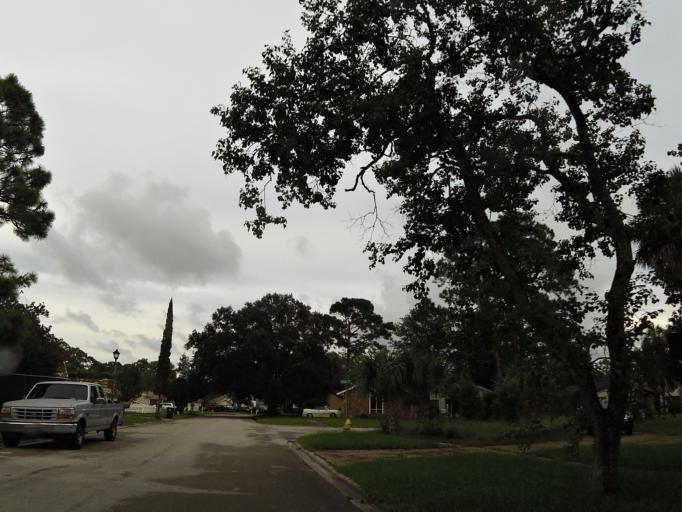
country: US
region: Florida
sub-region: Duval County
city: Neptune Beach
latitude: 30.3056
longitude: -81.5200
